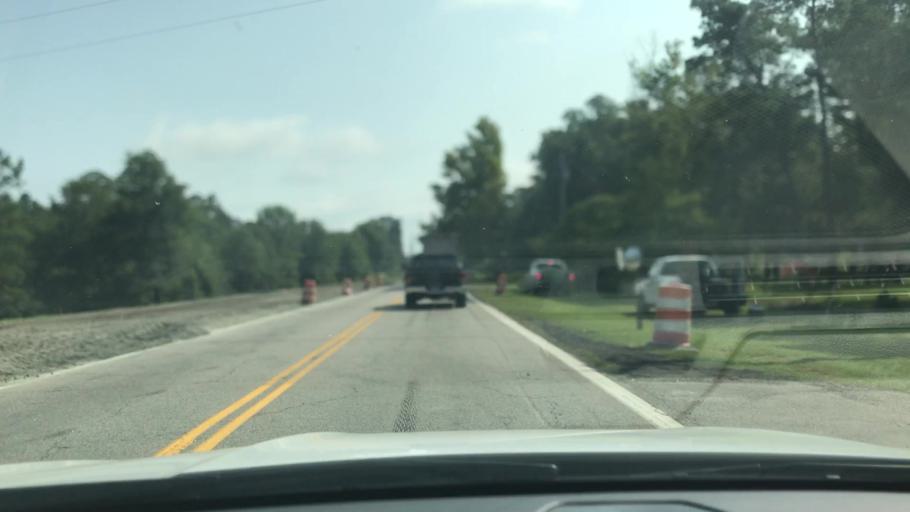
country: US
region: South Carolina
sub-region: Horry County
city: Socastee
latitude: 33.6700
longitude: -79.1409
